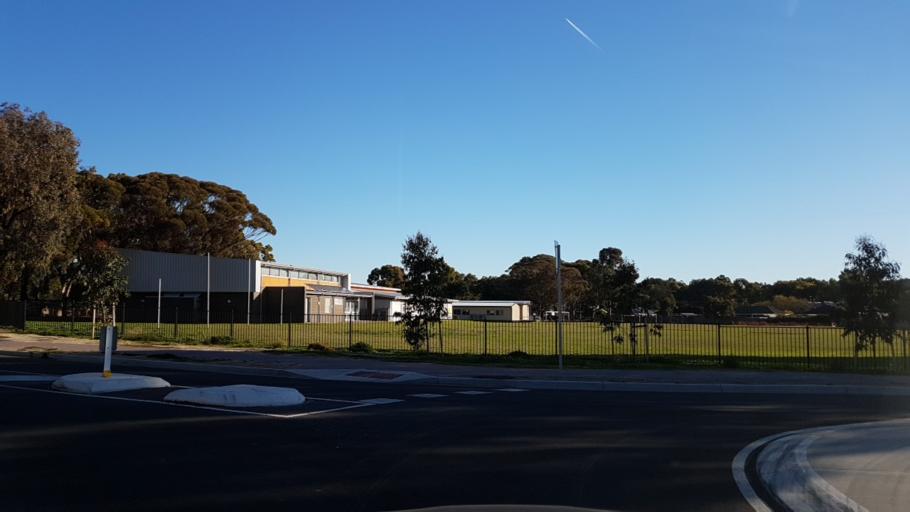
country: AU
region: South Australia
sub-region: Campbelltown
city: Hectorville
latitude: -34.8816
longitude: 138.6551
